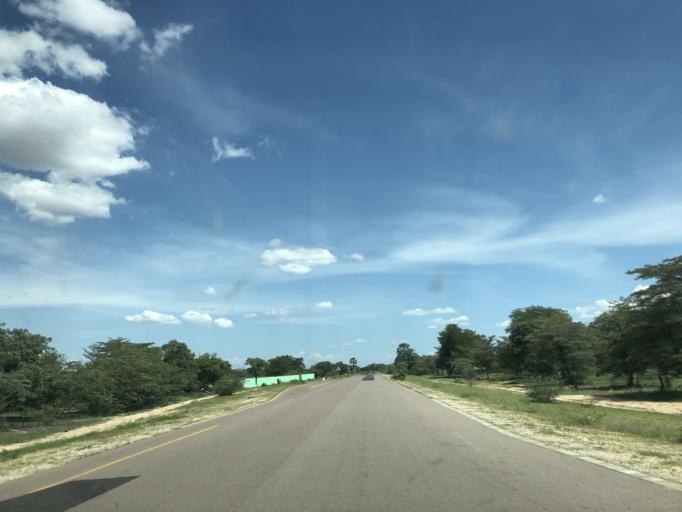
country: AO
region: Cunene
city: Ondjiva
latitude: -16.8807
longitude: 15.4875
